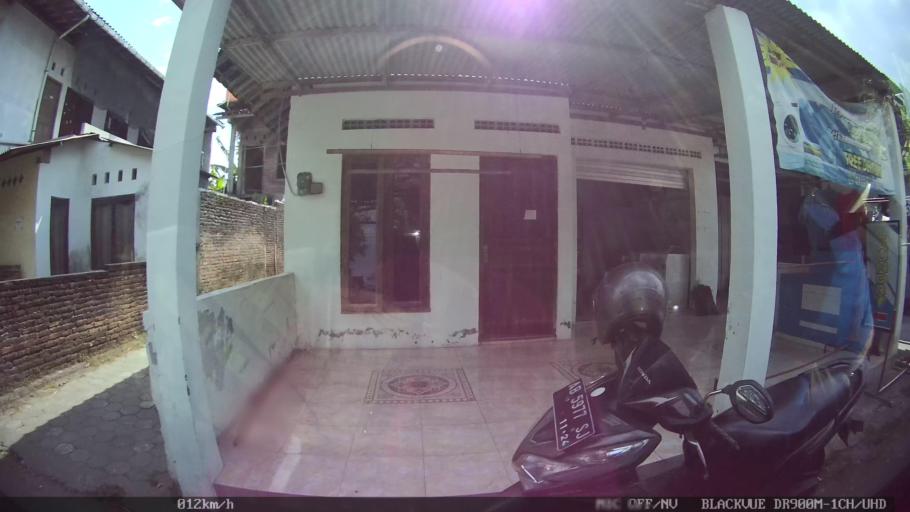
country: ID
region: Daerah Istimewa Yogyakarta
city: Kasihan
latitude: -7.8157
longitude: 110.3257
